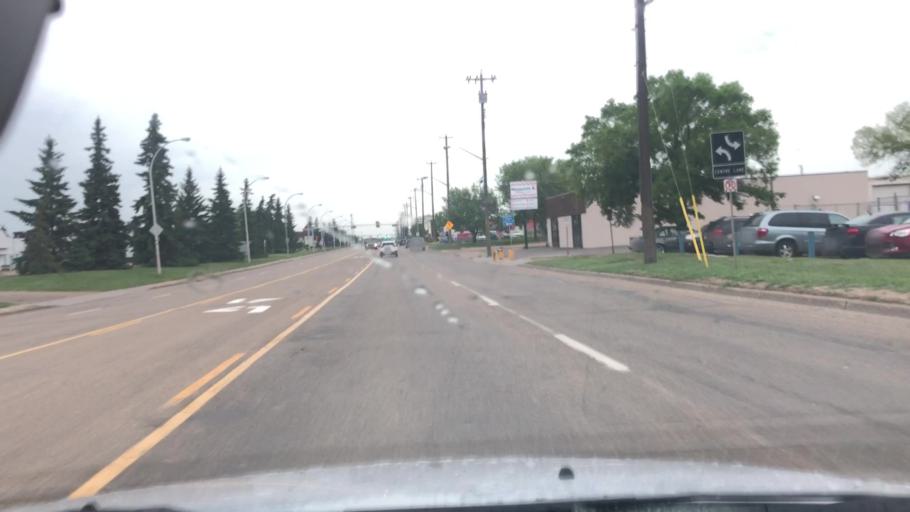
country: CA
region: Alberta
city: St. Albert
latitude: 53.5747
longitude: -113.5779
